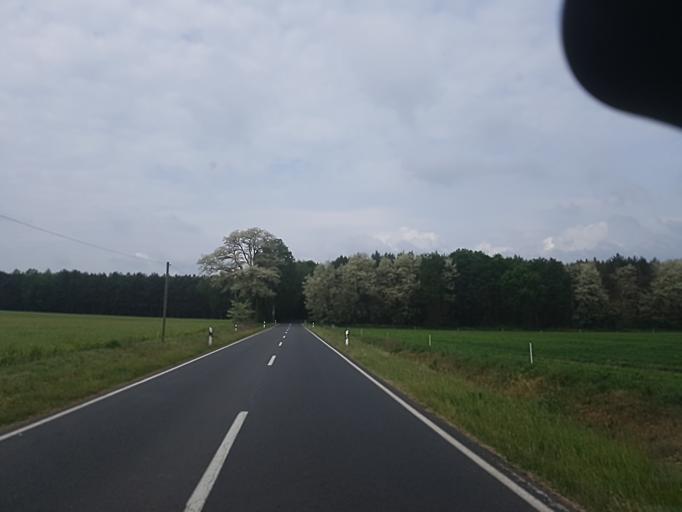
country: DE
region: Brandenburg
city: Gorzke
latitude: 52.0705
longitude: 12.2951
